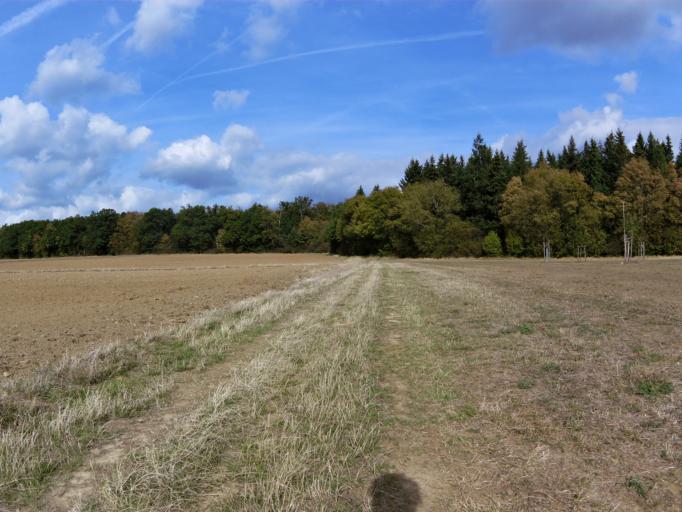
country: DE
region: Bavaria
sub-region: Regierungsbezirk Unterfranken
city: Reichenberg
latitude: 49.7340
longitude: 9.9436
